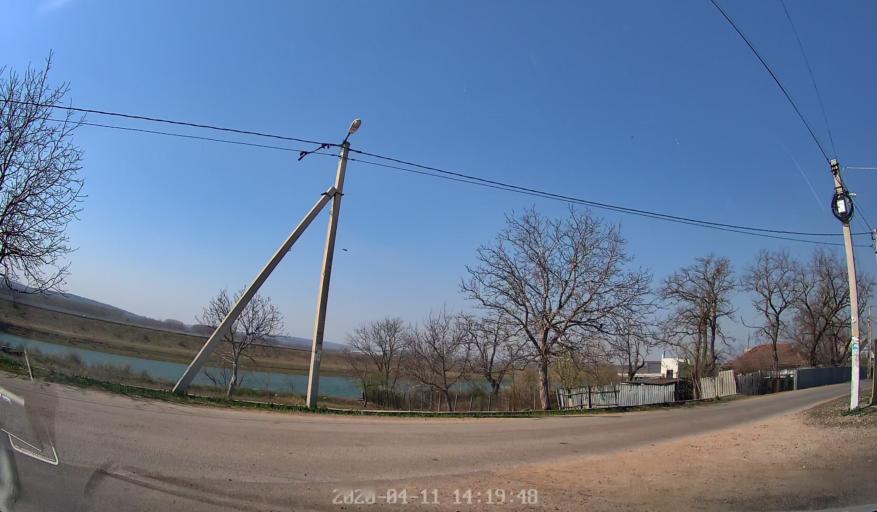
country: MD
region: Chisinau
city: Vadul lui Voda
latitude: 47.0850
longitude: 29.1314
